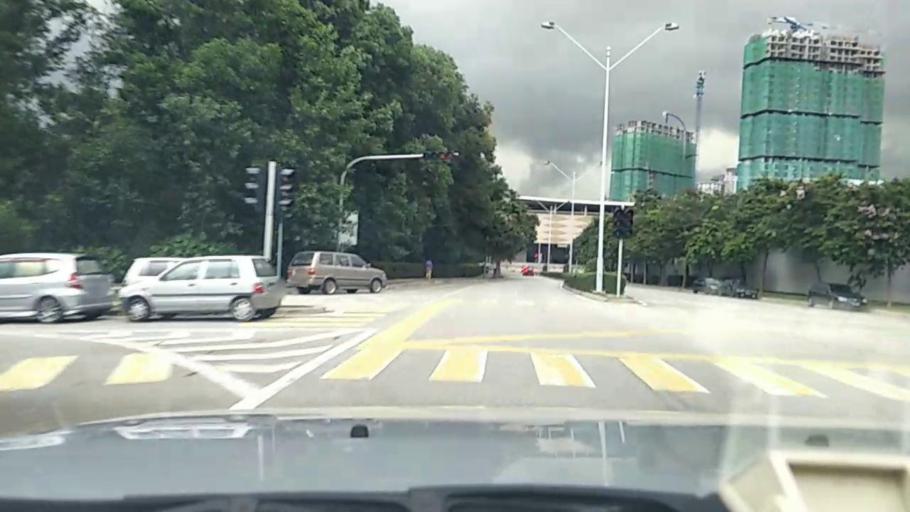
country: MY
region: Putrajaya
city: Putrajaya
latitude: 2.9364
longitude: 101.7104
